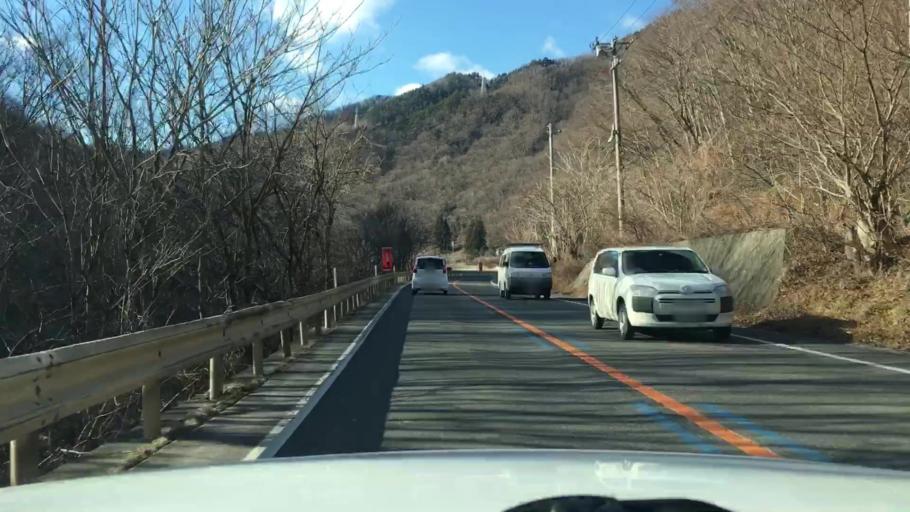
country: JP
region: Iwate
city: Miyako
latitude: 39.5990
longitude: 141.7375
